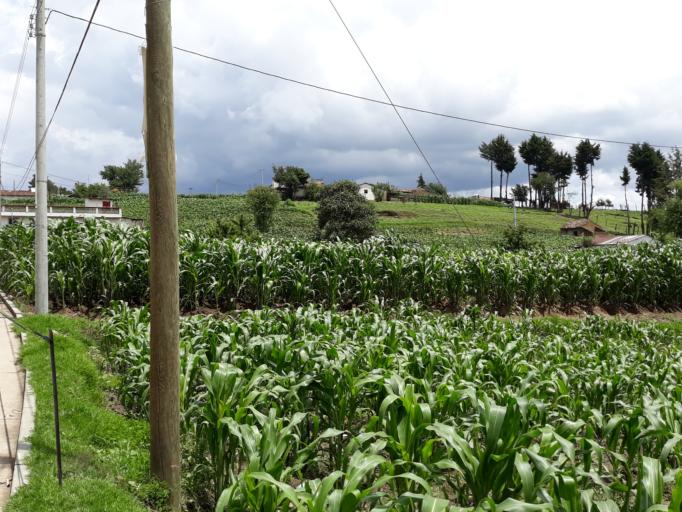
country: GT
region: Quetzaltenango
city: Salcaja
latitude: 14.8759
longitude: -91.4451
